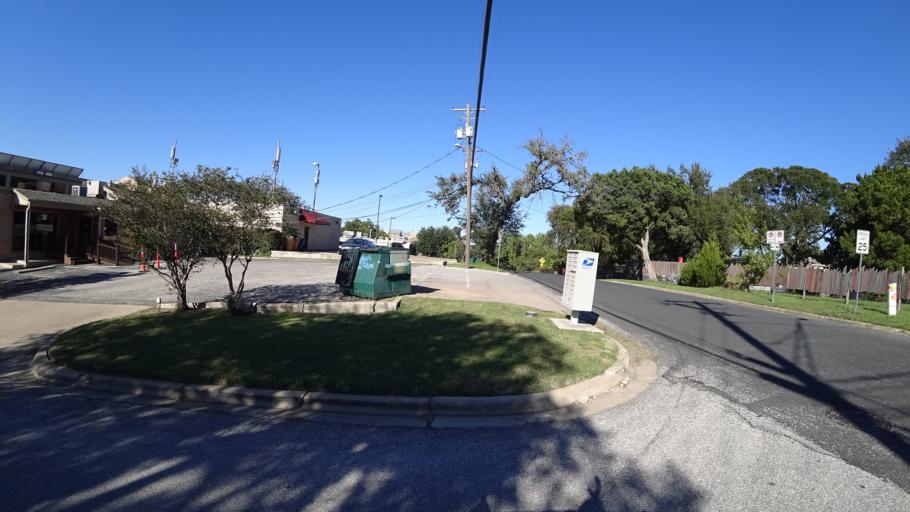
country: US
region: Texas
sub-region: Travis County
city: Austin
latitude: 30.2418
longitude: -97.7354
